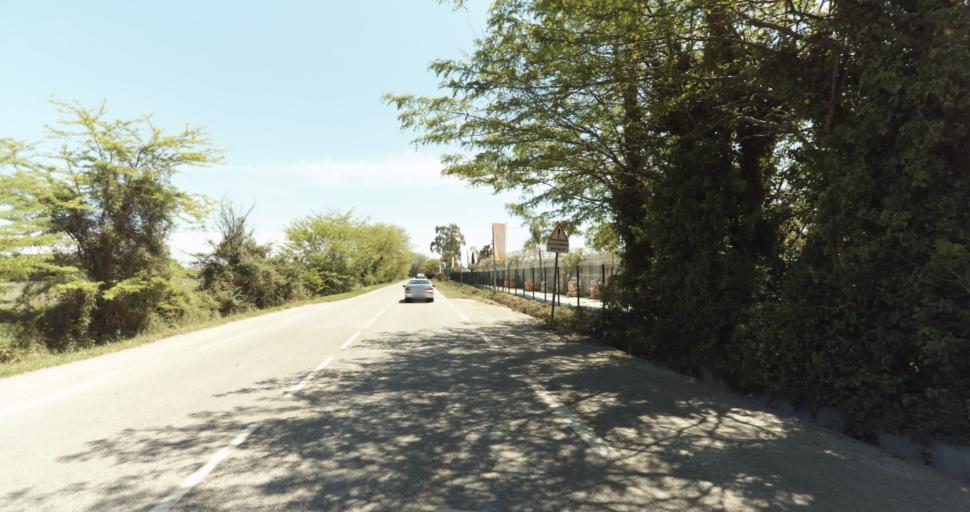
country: FR
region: Provence-Alpes-Cote d'Azur
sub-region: Departement du Var
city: Hyeres
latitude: 43.1407
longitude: 6.1546
